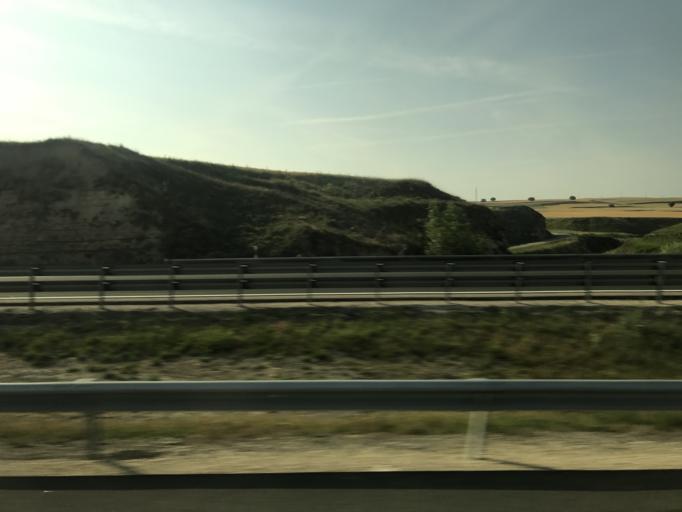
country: ES
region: Castille and Leon
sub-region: Provincia de Burgos
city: Briviesca
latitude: 42.5349
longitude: -3.3112
